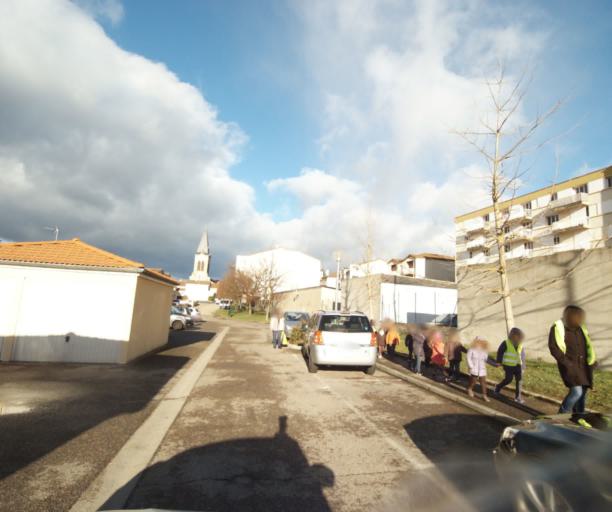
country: FR
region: Rhone-Alpes
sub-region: Departement de la Loire
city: La Talaudiere
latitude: 45.4788
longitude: 4.4321
